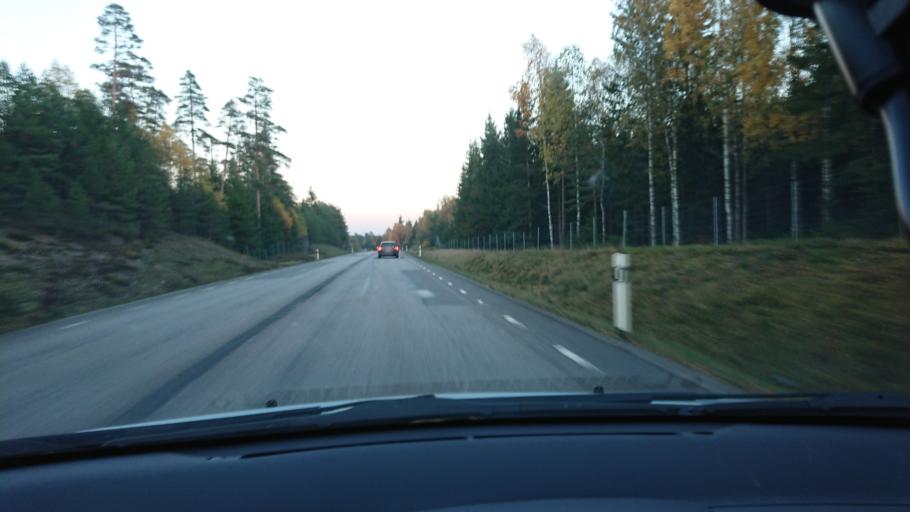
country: SE
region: Halland
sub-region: Laholms Kommun
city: Knared
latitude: 56.7273
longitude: 13.3932
